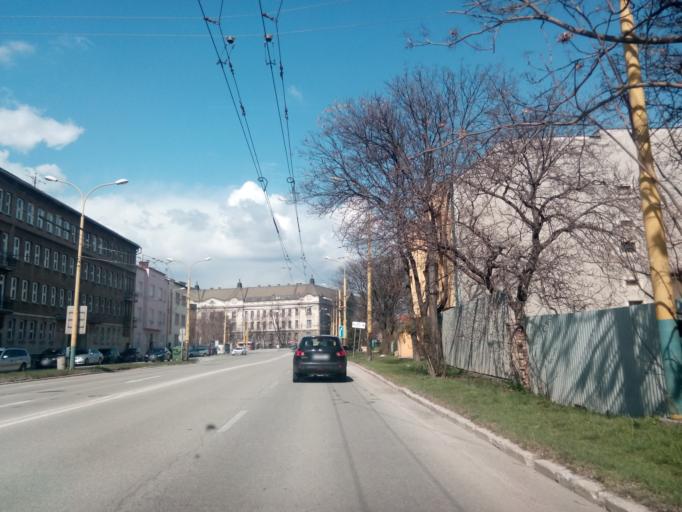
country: SK
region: Kosicky
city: Kosice
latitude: 48.7264
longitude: 21.2587
